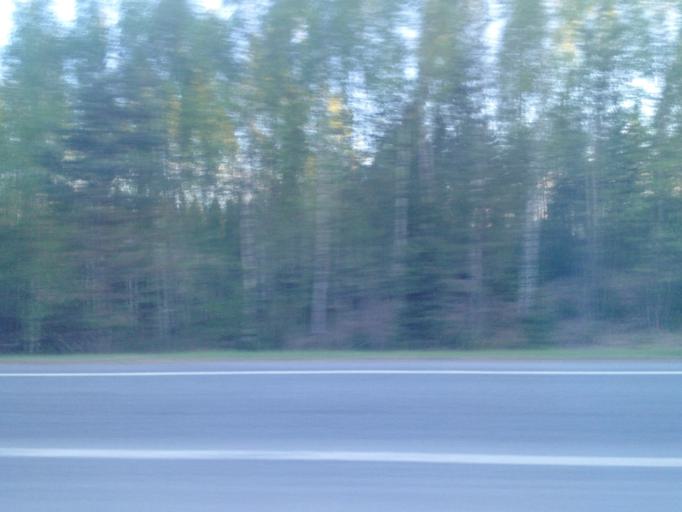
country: FI
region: Haeme
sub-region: Haemeenlinna
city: Janakkala
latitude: 60.9129
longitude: 24.5410
